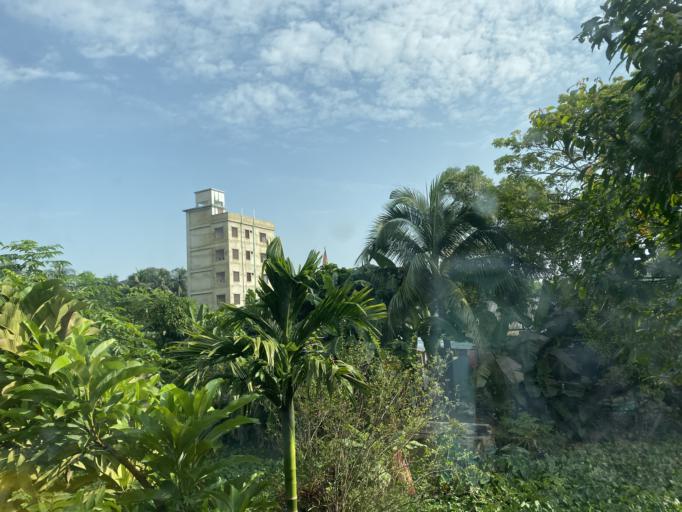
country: BD
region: Dhaka
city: Bhairab Bazar
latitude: 23.9661
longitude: 91.1164
